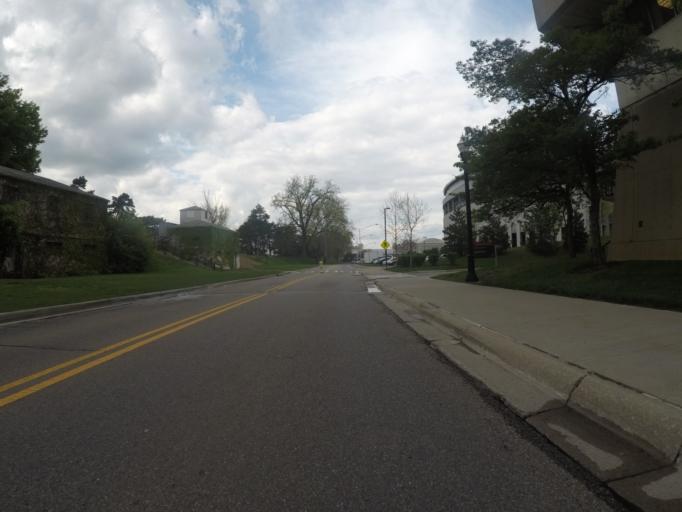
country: US
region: Ohio
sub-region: Franklin County
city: Grandview Heights
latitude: 40.0002
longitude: -83.0222
